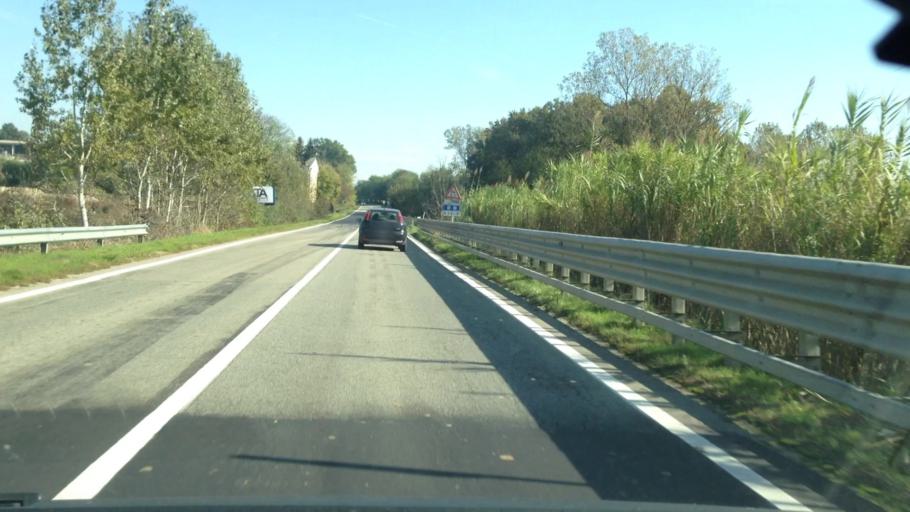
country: IT
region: Piedmont
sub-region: Provincia di Asti
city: Castello di Annone
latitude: 44.8785
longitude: 8.3295
